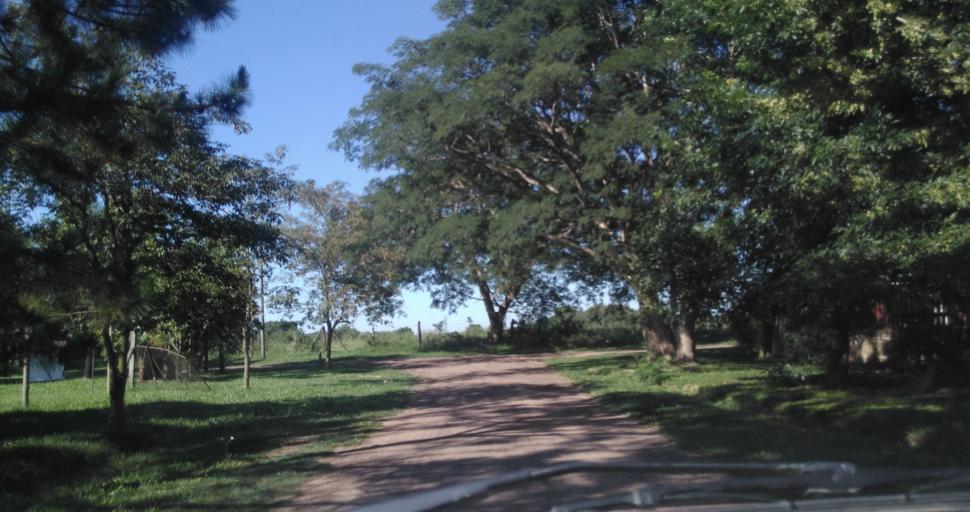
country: AR
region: Chaco
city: Resistencia
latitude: -27.4389
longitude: -58.9528
